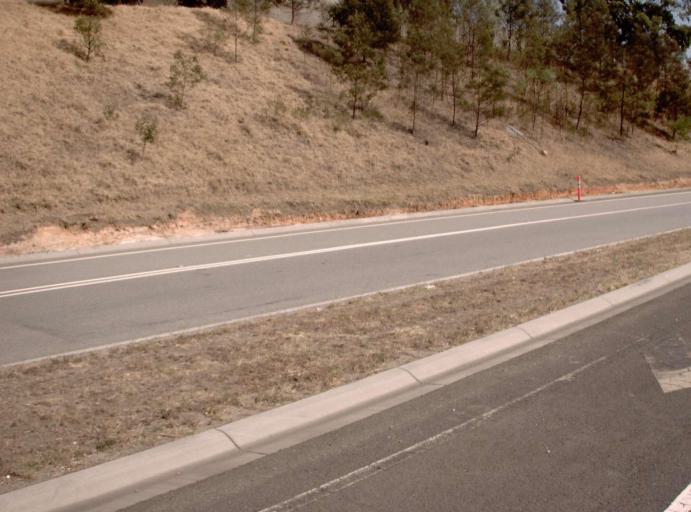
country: AU
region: Victoria
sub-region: Casey
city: Eumemmerring
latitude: -38.0012
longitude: 145.2521
